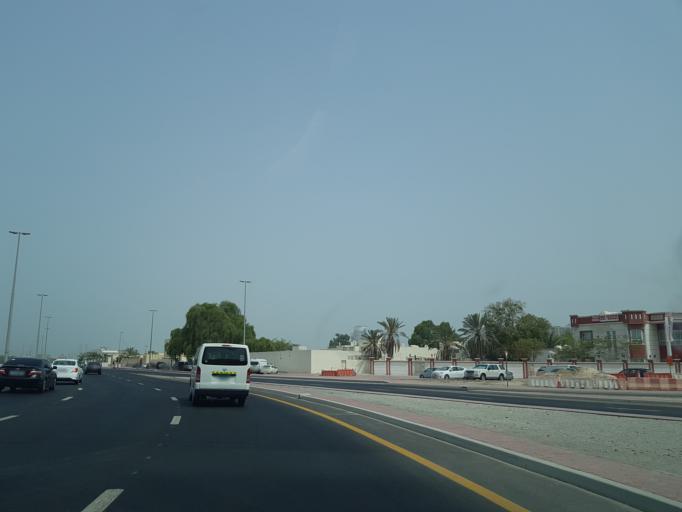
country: AE
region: Ash Shariqah
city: Sharjah
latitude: 25.2396
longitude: 55.2950
